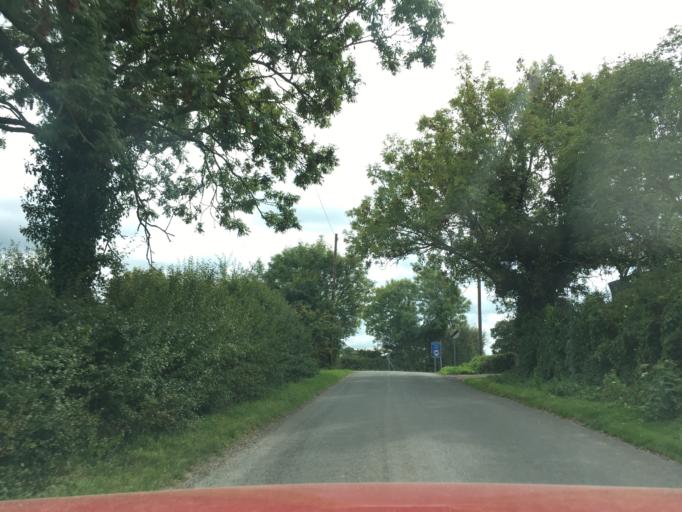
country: GB
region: England
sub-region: South Gloucestershire
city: Charfield
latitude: 51.6605
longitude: -2.4174
